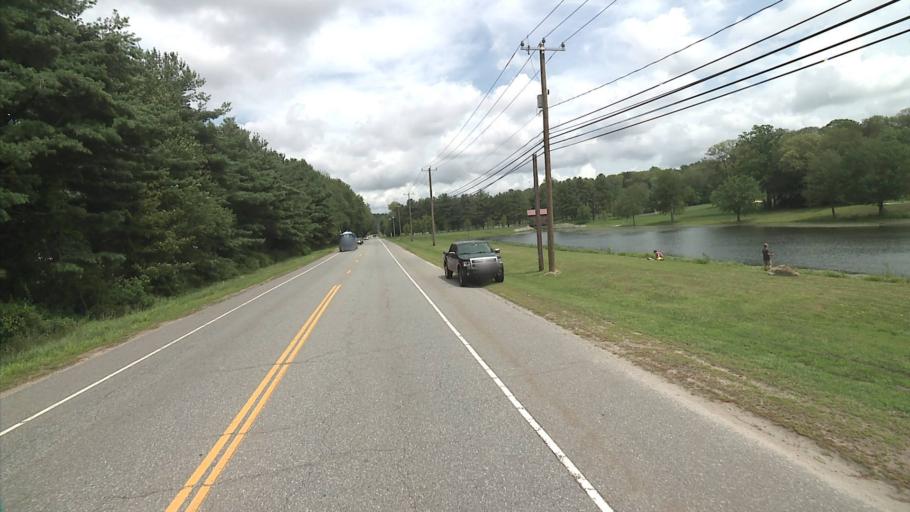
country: US
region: Connecticut
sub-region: Middlesex County
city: Deep River Center
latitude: 41.3666
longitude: -72.4633
